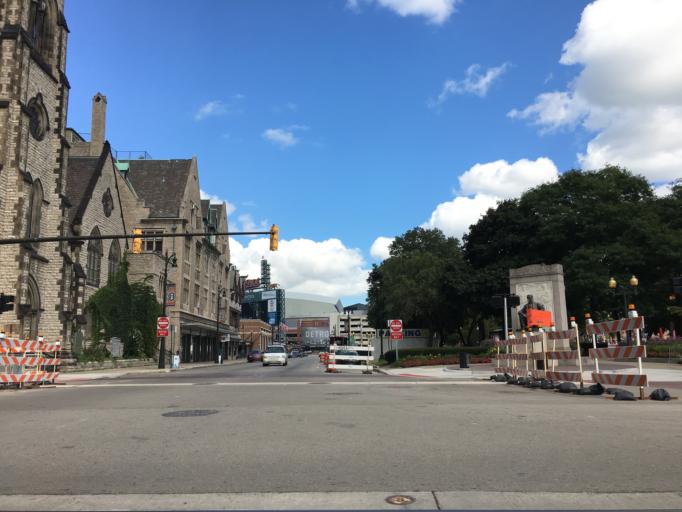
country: US
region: Michigan
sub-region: Wayne County
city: Detroit
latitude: 42.3370
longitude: -83.0510
